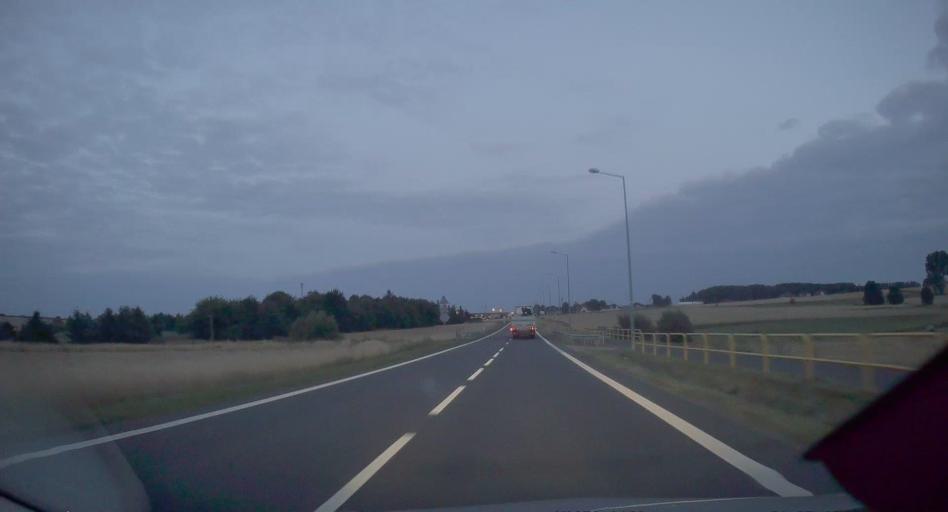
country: PL
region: Silesian Voivodeship
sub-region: Powiat klobucki
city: Opatow
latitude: 50.9332
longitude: 18.8540
